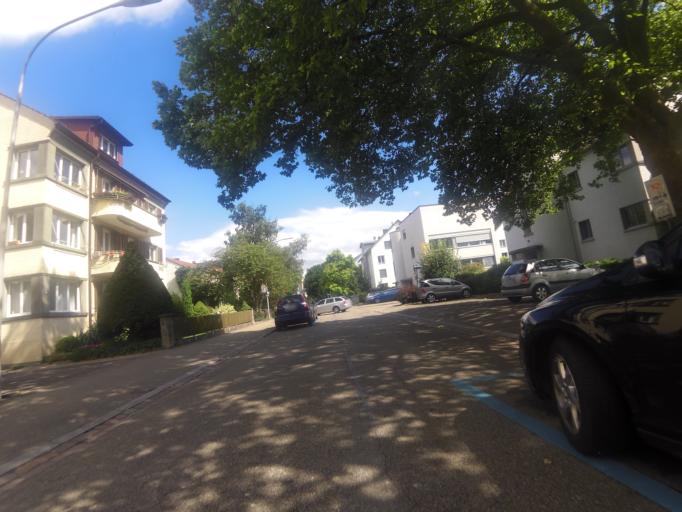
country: CH
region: Zurich
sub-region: Bezirk Zuerich
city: Zuerich (Kreis 9) / Albisrieden
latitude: 47.3770
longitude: 8.4928
